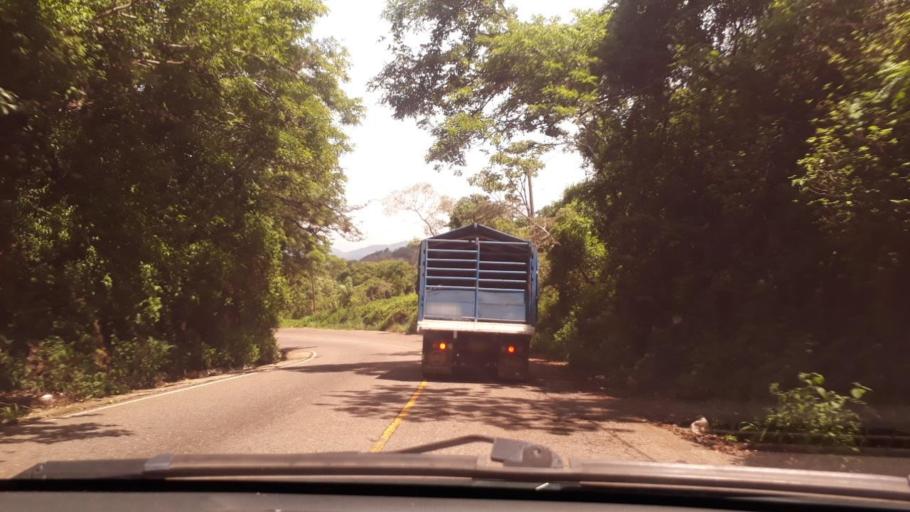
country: GT
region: Jutiapa
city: Jalpatagua
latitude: 14.1784
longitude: -90.0489
